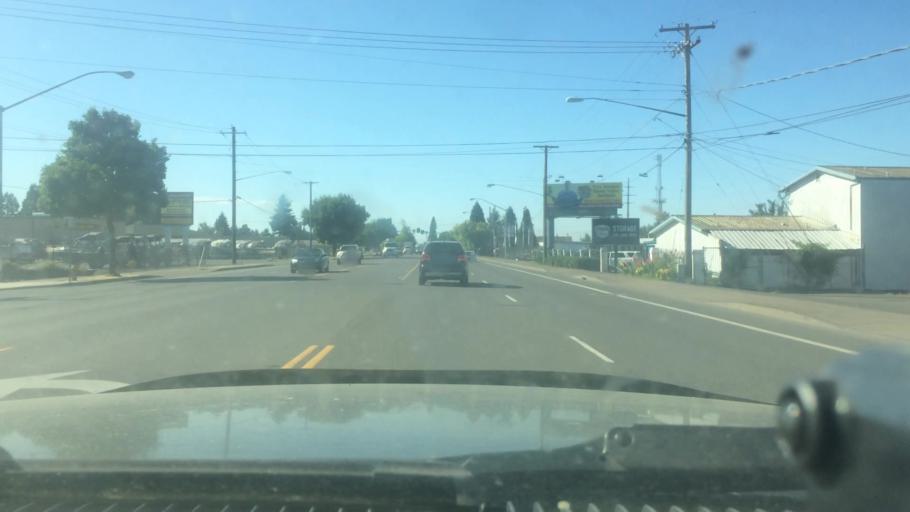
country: US
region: Oregon
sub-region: Lane County
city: Eugene
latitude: 44.0785
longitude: -123.1501
